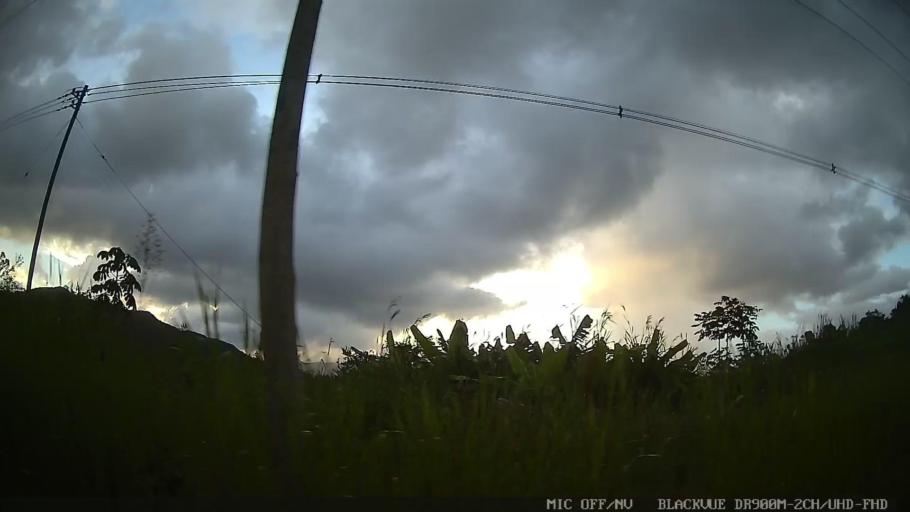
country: BR
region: Sao Paulo
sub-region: Itanhaem
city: Itanhaem
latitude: -24.0946
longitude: -46.7992
